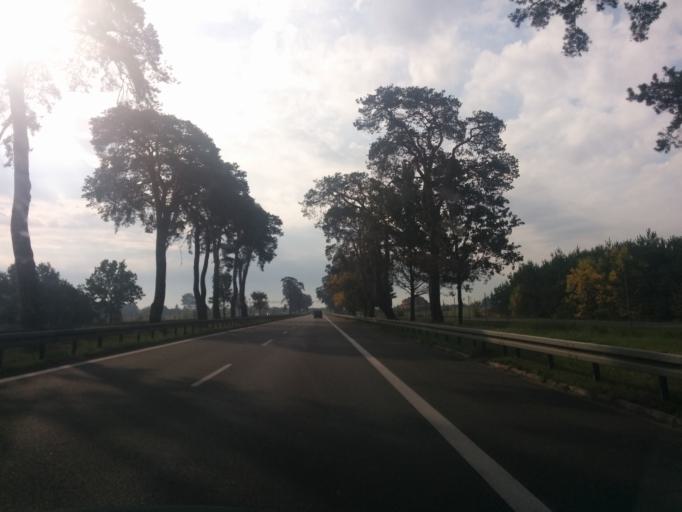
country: PL
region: Masovian Voivodeship
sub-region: Powiat bialobrzeski
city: Stara Blotnica
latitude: 51.5927
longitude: 20.9937
